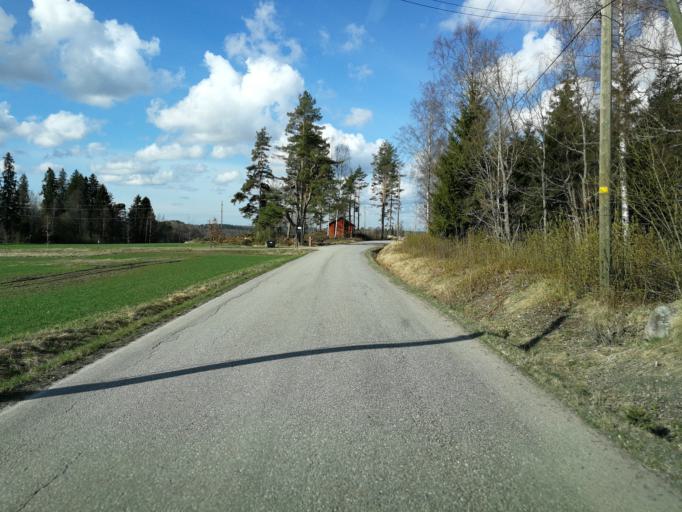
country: FI
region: Uusimaa
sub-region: Helsinki
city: Lohja
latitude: 60.1549
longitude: 24.1074
